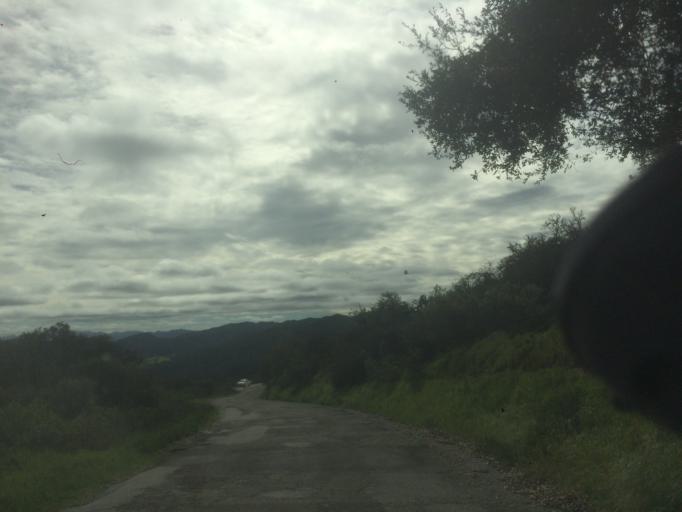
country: US
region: California
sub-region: San Luis Obispo County
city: Nipomo
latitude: 35.1941
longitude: -120.4454
